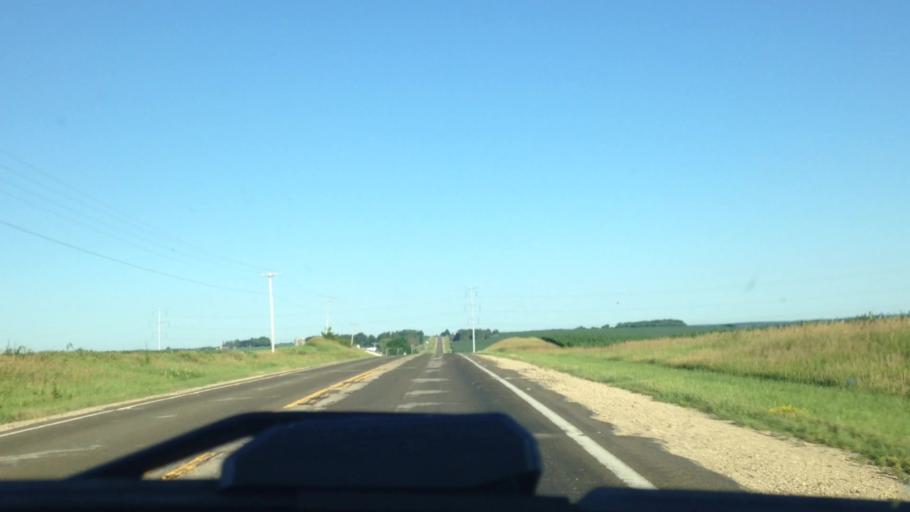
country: US
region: Wisconsin
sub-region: Columbia County
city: Poynette
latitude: 43.3377
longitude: -89.3960
